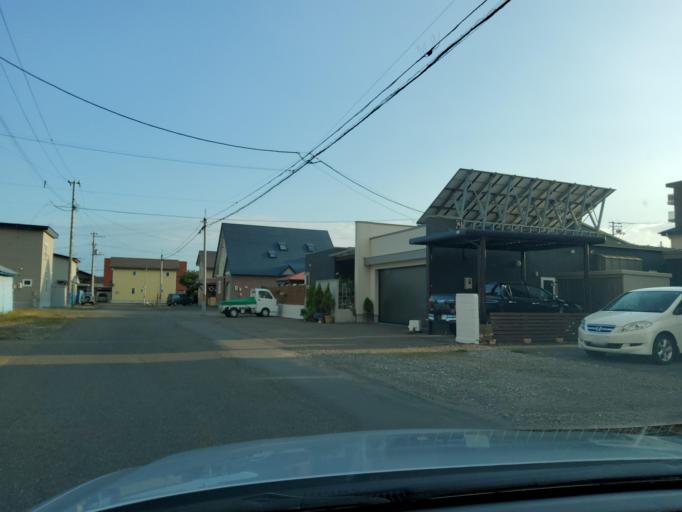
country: JP
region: Hokkaido
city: Obihiro
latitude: 42.9189
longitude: 143.1701
